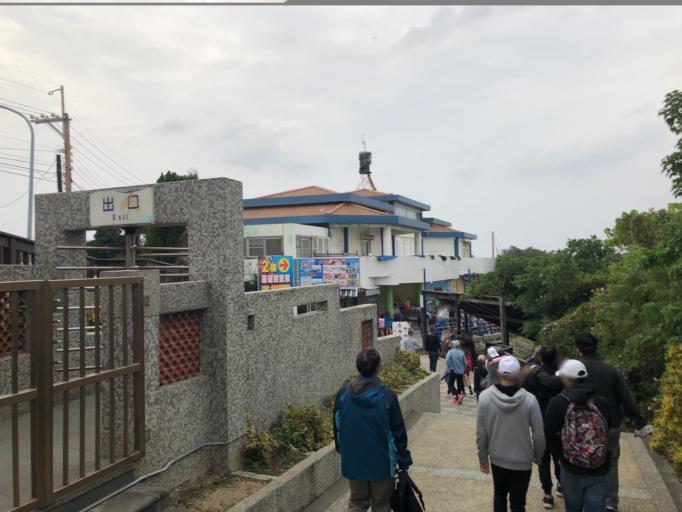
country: TW
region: Kaohsiung
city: Kaohsiung
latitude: 22.3296
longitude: 120.3553
